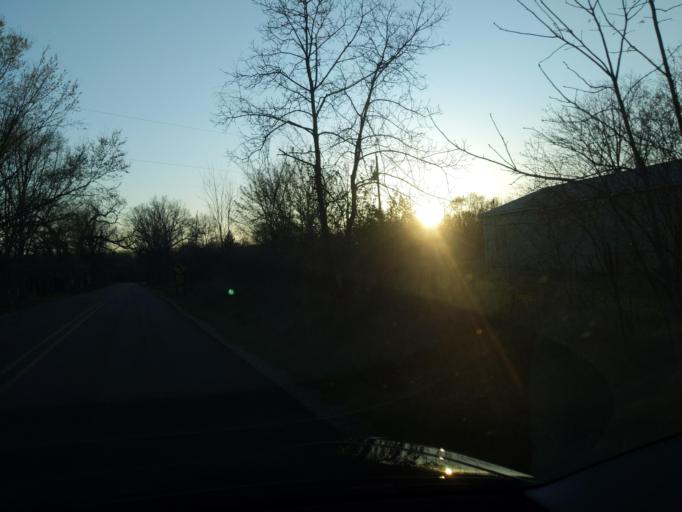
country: US
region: Michigan
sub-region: Ingham County
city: Stockbridge
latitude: 42.4997
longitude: -84.2746
